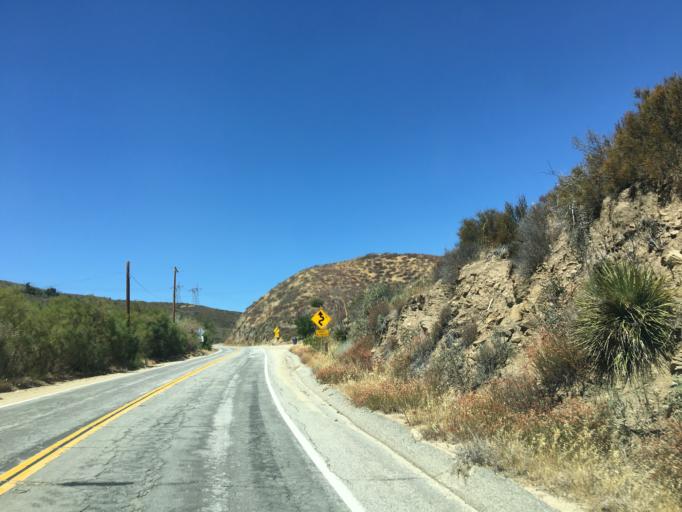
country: US
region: California
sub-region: Los Angeles County
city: Leona Valley
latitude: 34.5877
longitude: -118.2915
